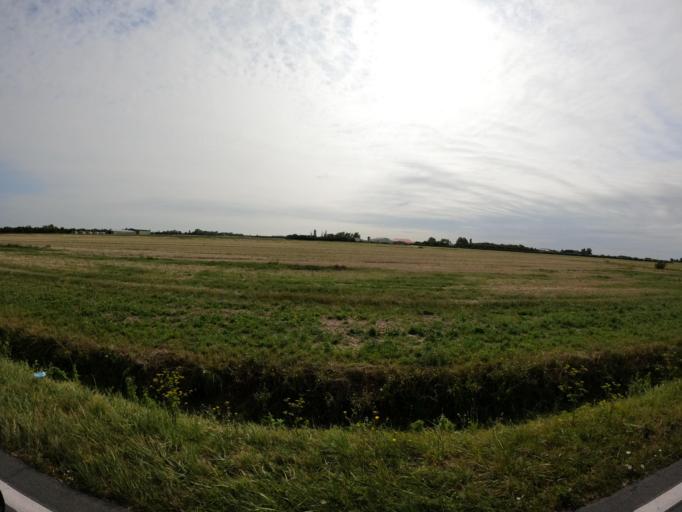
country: FR
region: Pays de la Loire
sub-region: Departement de la Vendee
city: Triaize
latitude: 46.3834
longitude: -1.2024
